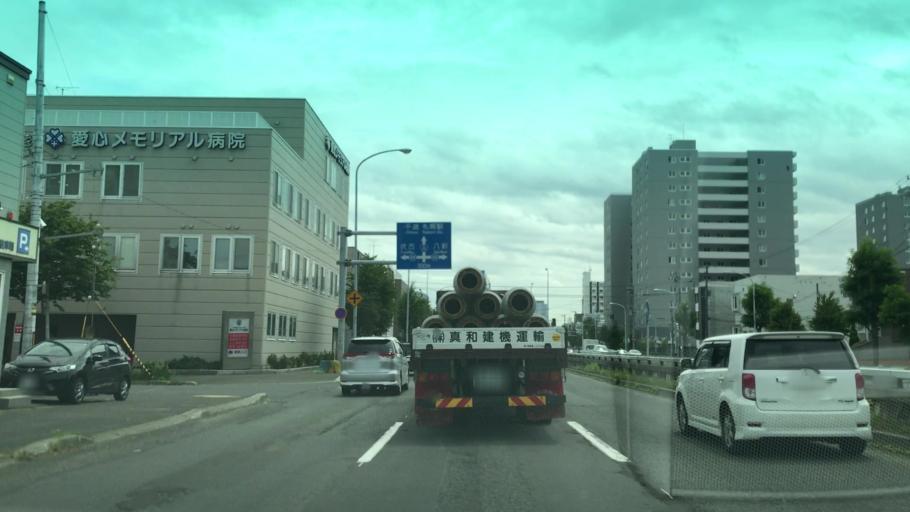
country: JP
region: Hokkaido
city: Sapporo
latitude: 43.0944
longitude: 141.3469
